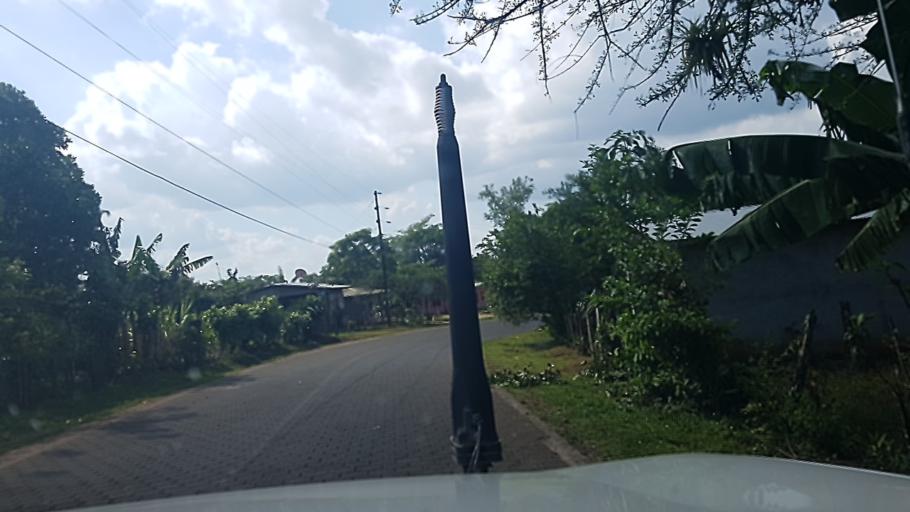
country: NI
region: Atlantico Sur
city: Nueva Guinea
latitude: 11.7025
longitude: -84.3766
